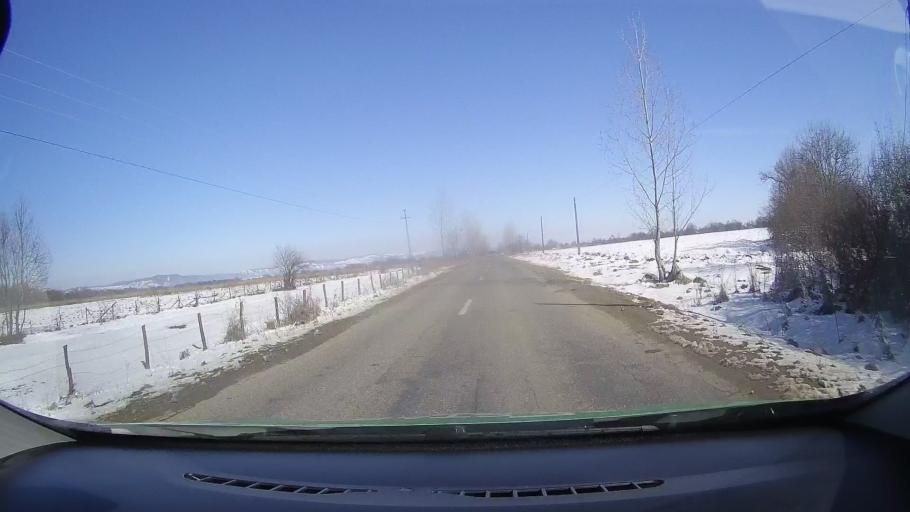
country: RO
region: Brasov
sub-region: Oras Victoria
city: Victoria
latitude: 45.7374
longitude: 24.7334
